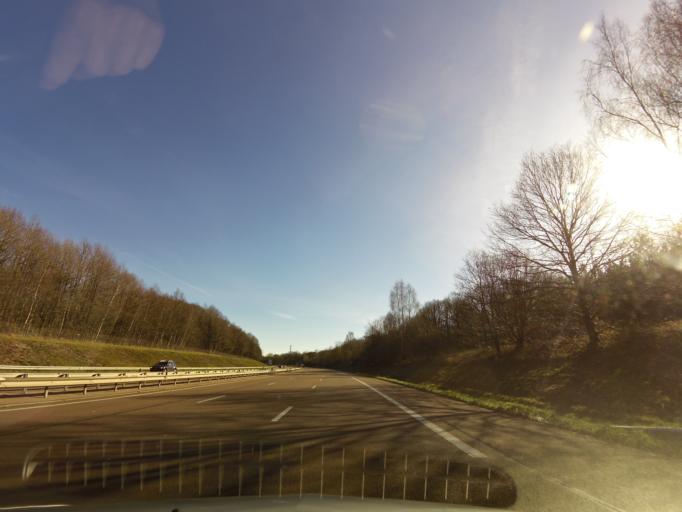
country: FR
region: Bourgogne
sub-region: Departement de l'Yonne
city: Aillant-sur-Tholon
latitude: 47.9158
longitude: 3.2892
